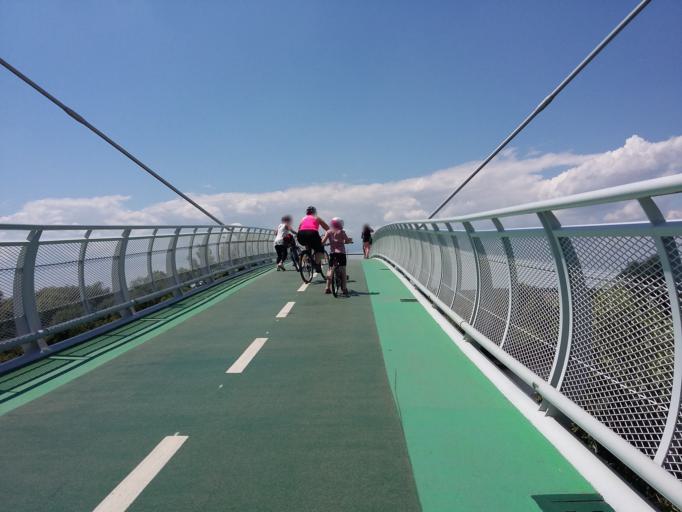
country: AT
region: Lower Austria
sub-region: Politischer Bezirk Bruck an der Leitha
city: Hainburg an der Donau
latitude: 48.2111
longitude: 16.9654
